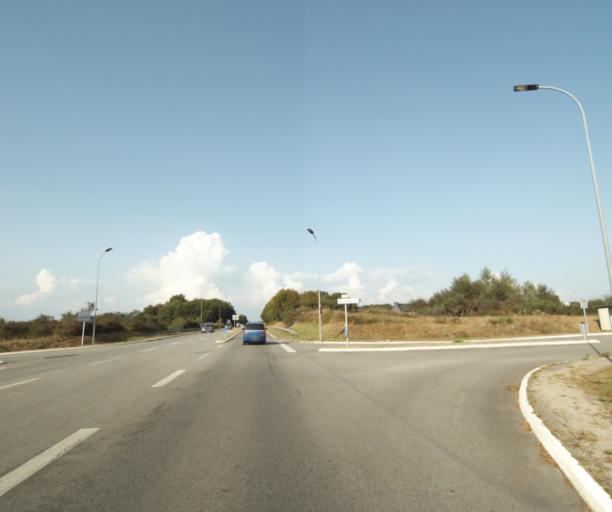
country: FR
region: Brittany
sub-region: Departement du Morbihan
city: Riantec
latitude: 47.7511
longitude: -3.2912
